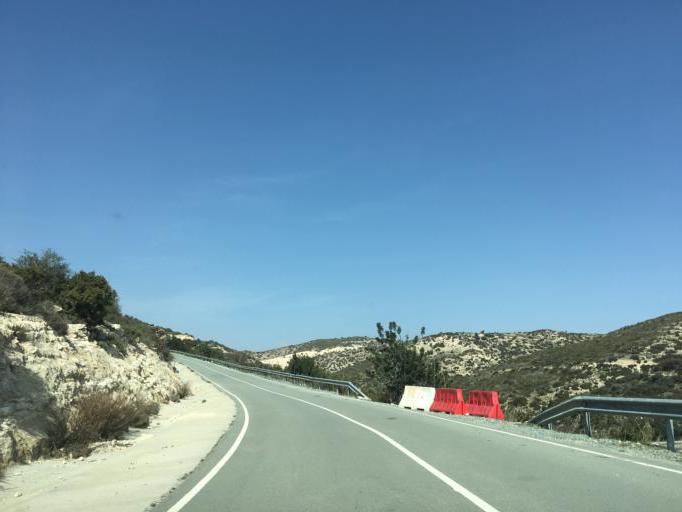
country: CY
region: Limassol
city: Pano Polemidia
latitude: 34.7688
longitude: 32.9367
